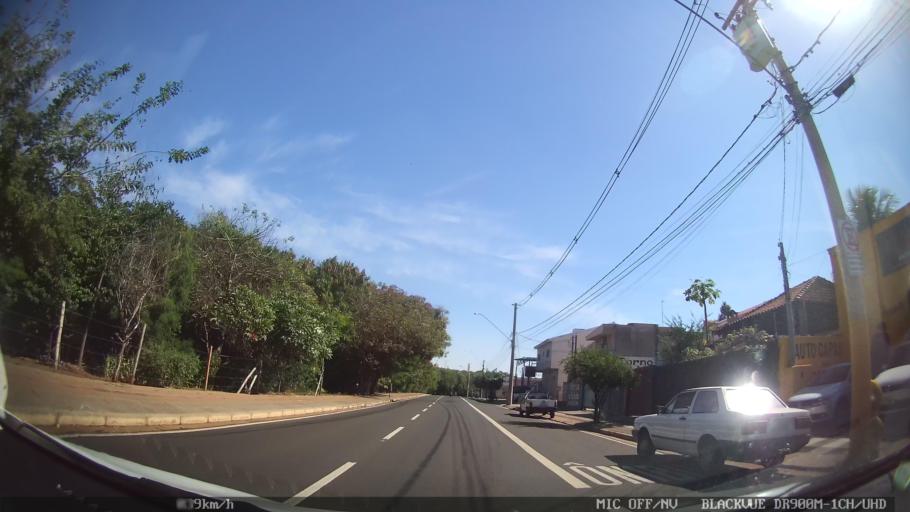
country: BR
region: Sao Paulo
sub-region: Sao Jose Do Rio Preto
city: Sao Jose do Rio Preto
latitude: -20.7770
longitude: -49.3941
